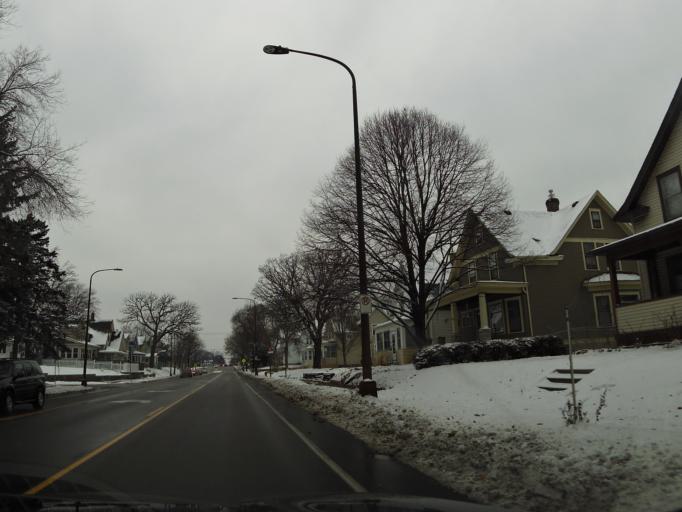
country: US
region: Minnesota
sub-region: Ramsey County
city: Saint Paul
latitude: 44.9775
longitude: -93.0686
